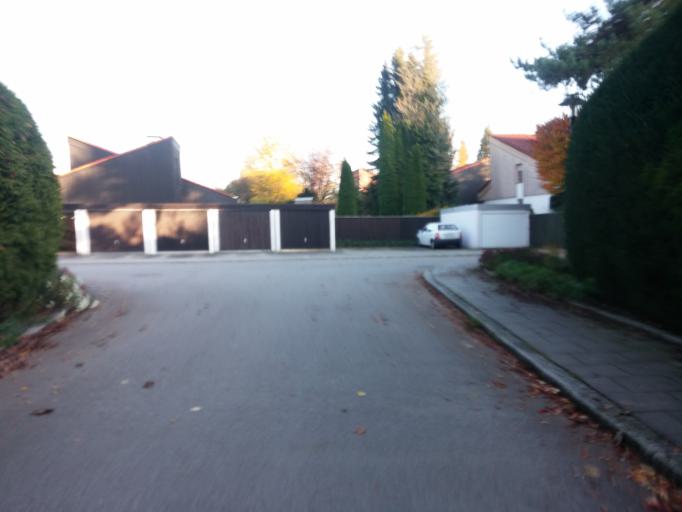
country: DE
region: Bavaria
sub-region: Upper Bavaria
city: Vaterstetten
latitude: 48.0915
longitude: 11.7951
